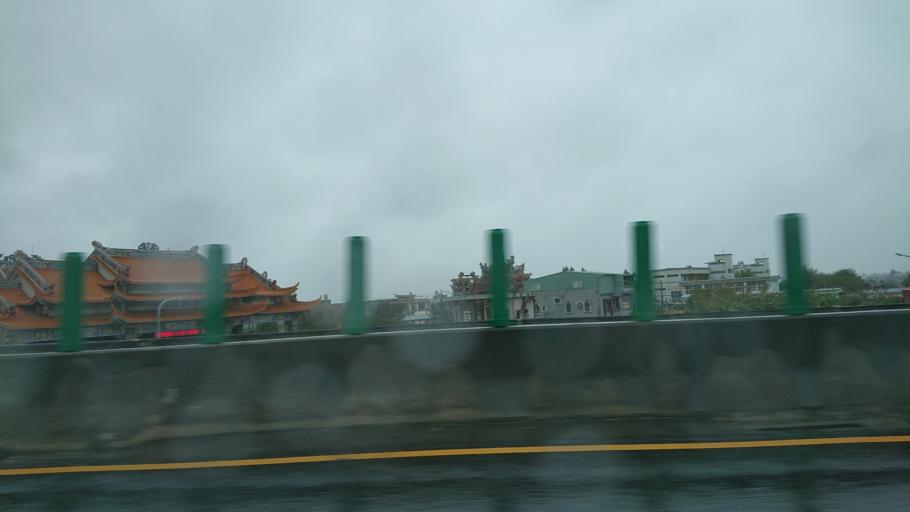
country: TW
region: Taiwan
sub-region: Chiayi
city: Taibao
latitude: 23.5737
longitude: 120.1518
